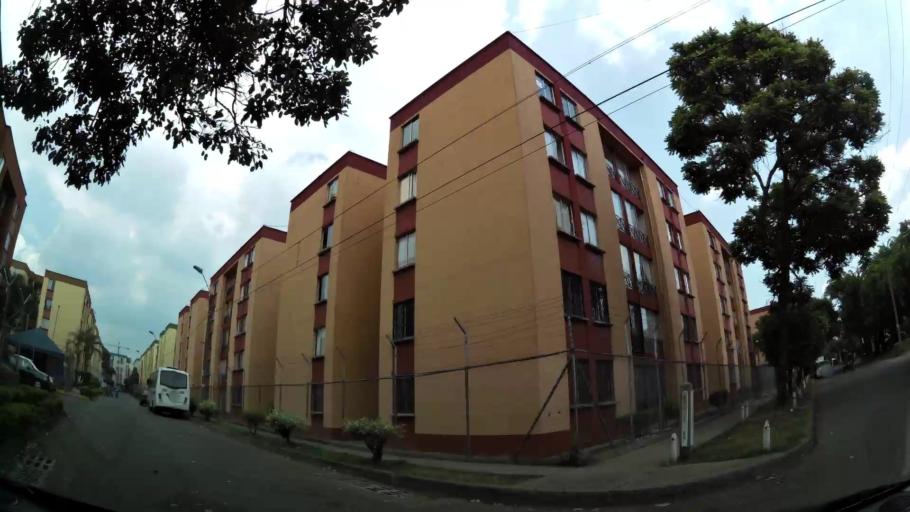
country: CO
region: Valle del Cauca
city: Cali
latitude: 3.4747
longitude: -76.4992
